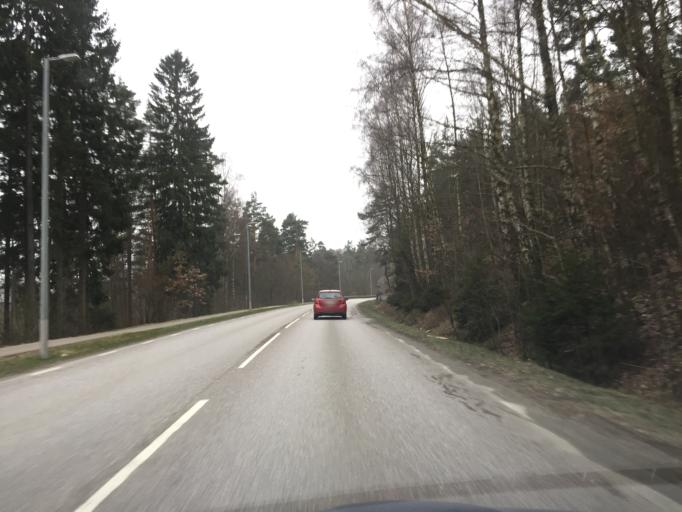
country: SE
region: Vaestra Goetaland
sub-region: Goteborg
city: Eriksbo
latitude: 57.7671
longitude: 12.0747
